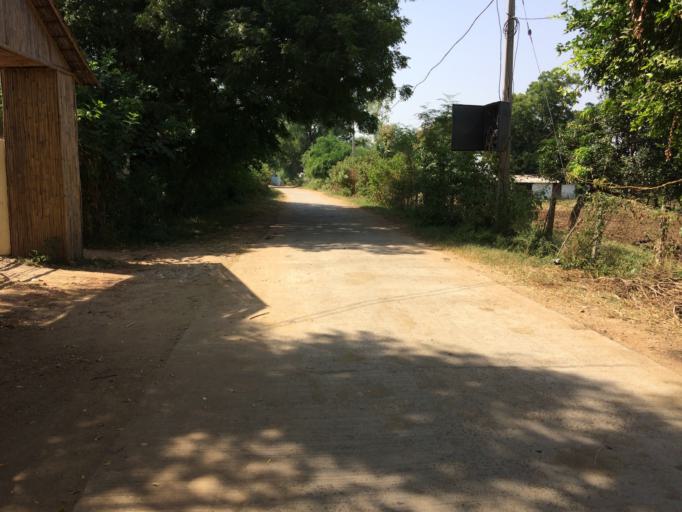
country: IN
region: Madhya Pradesh
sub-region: Dewas
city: Khategaon
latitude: 22.4954
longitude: 76.9310
